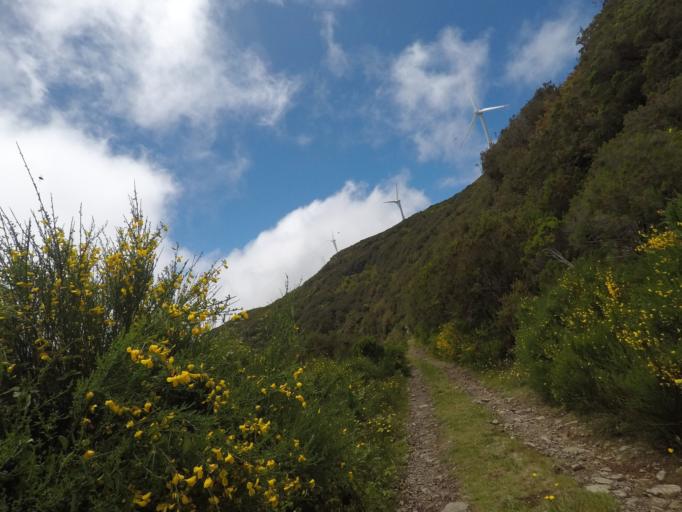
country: PT
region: Madeira
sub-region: Sao Vicente
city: Sao Vicente
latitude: 32.7700
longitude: -17.0690
